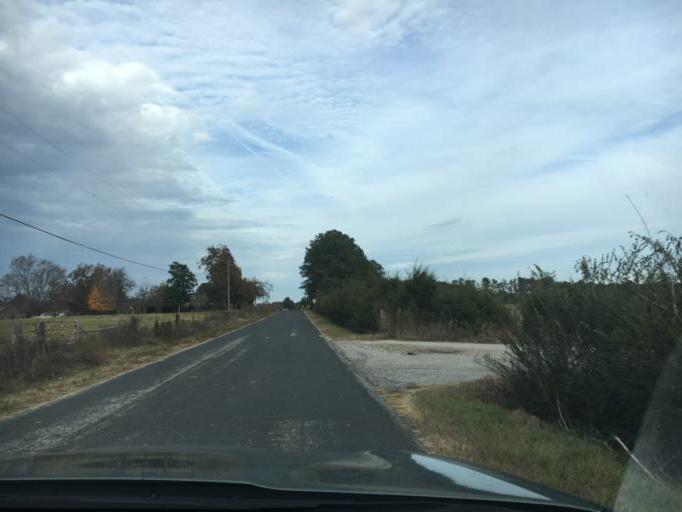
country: US
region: South Carolina
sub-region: Laurens County
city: Watts Mills
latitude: 34.5285
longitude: -81.9352
